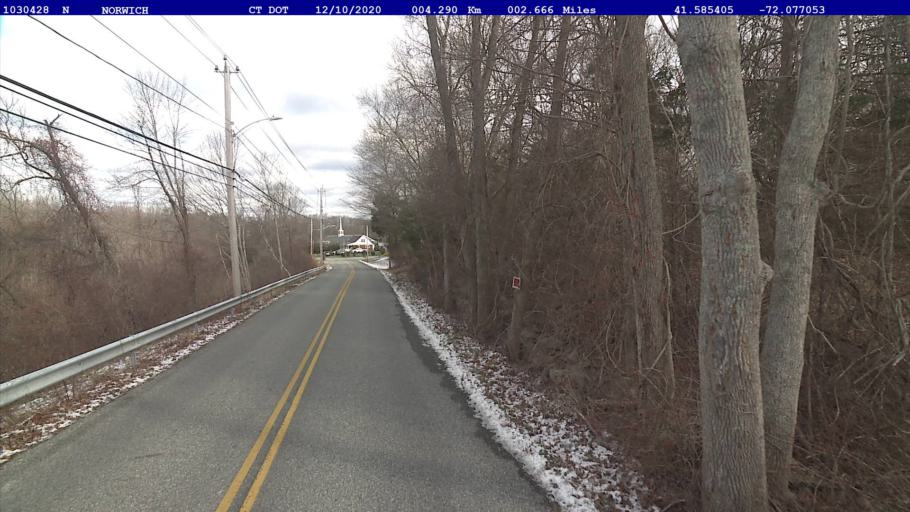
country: US
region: Connecticut
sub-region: New London County
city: Baltic
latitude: 41.5854
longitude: -72.0770
